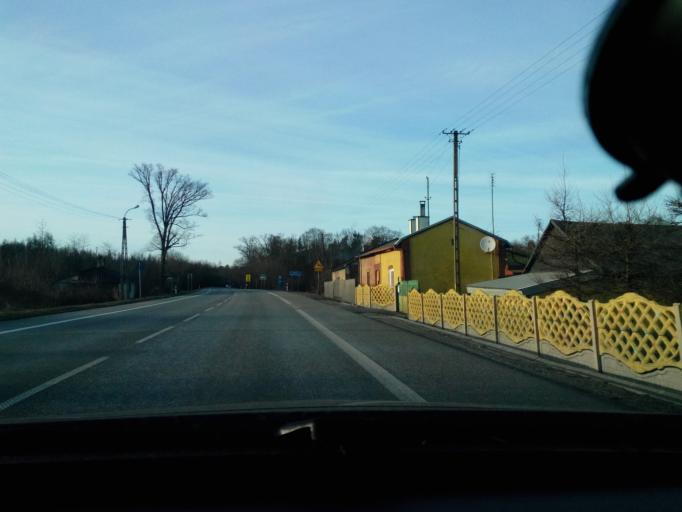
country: PL
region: Lodz Voivodeship
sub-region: Powiat kutnowski
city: Ostrowy
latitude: 52.2813
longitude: 19.1628
